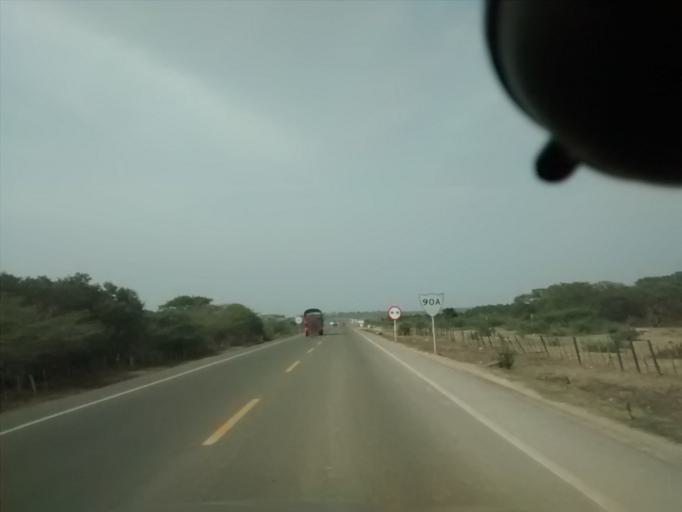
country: CO
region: Bolivar
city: Cartagena
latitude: 10.4974
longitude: -75.4782
